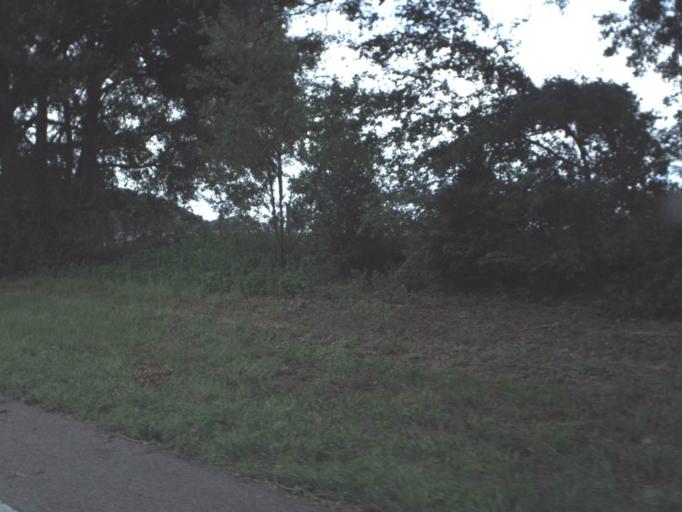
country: US
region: Florida
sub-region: Gilchrist County
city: Trenton
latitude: 29.6693
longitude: -82.8524
